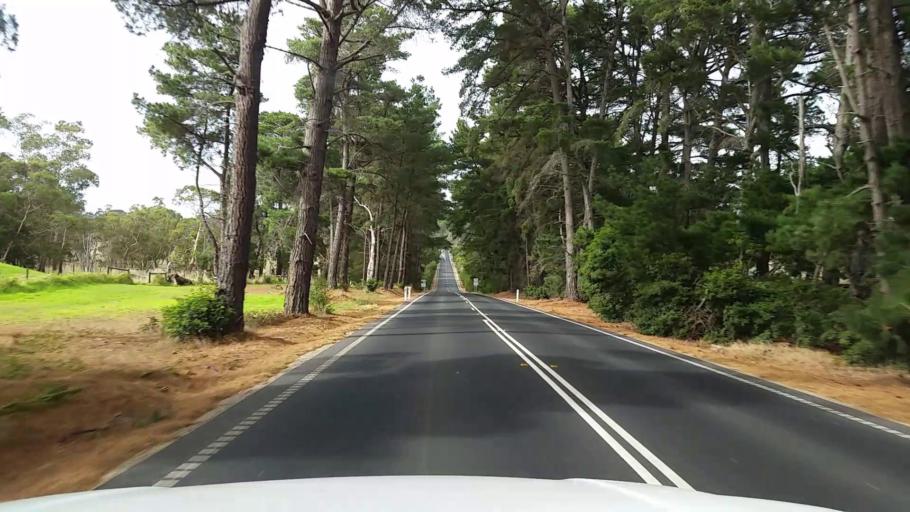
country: AU
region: Victoria
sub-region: Mornington Peninsula
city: Balnarring
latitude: -38.3585
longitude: 145.1120
